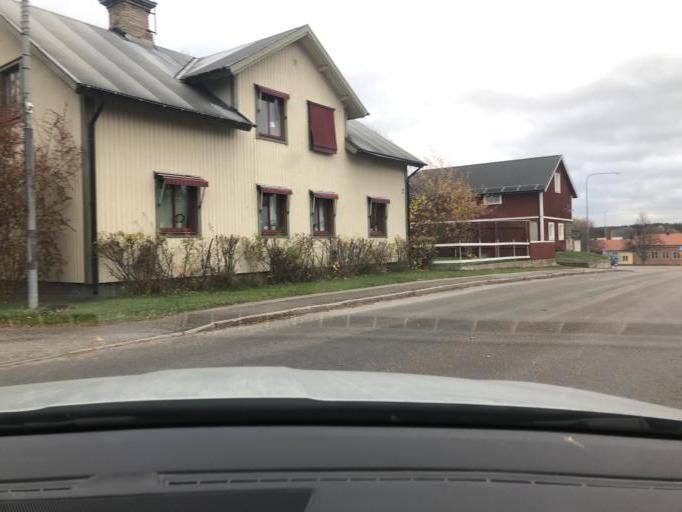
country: SE
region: Uppsala
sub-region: Tierps Kommun
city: Tierp
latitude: 60.3441
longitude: 17.5200
